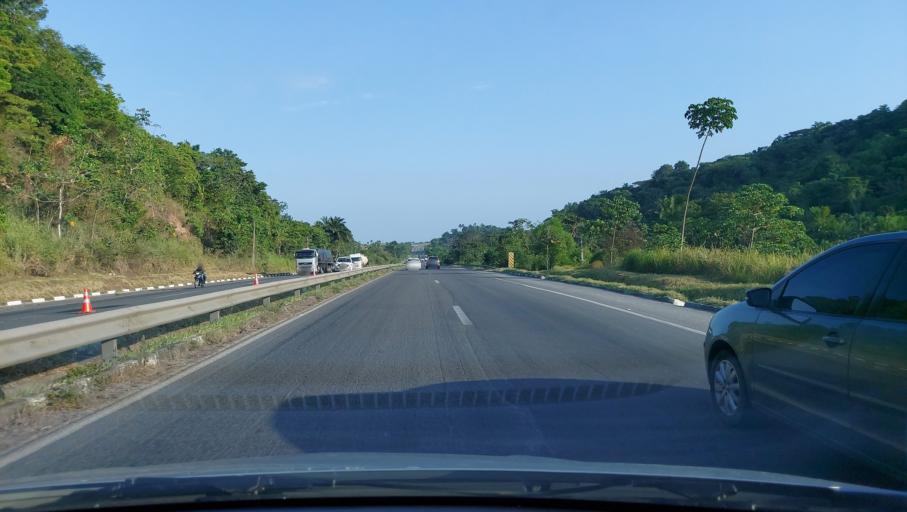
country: BR
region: Bahia
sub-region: Santo Amaro
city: Santo Amaro
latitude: -12.4356
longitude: -38.7283
